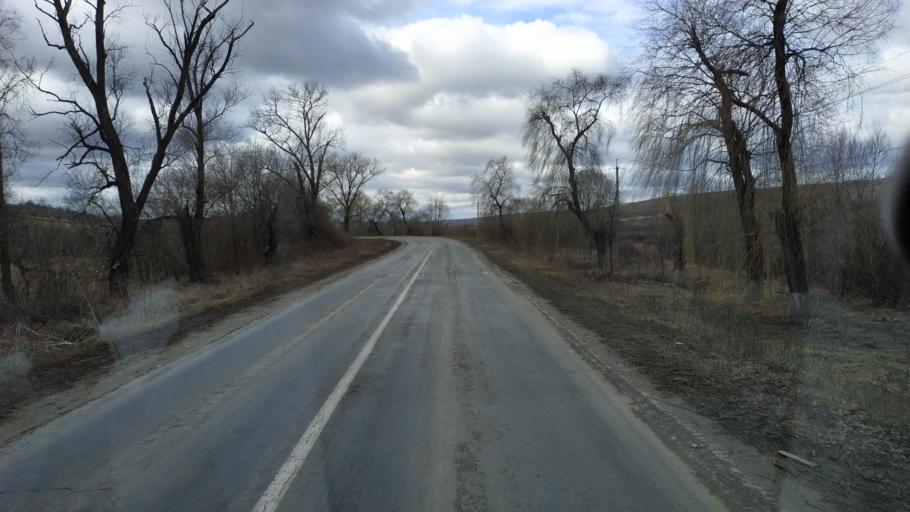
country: MD
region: Stinga Nistrului
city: Bucovat
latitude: 47.1501
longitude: 28.4078
